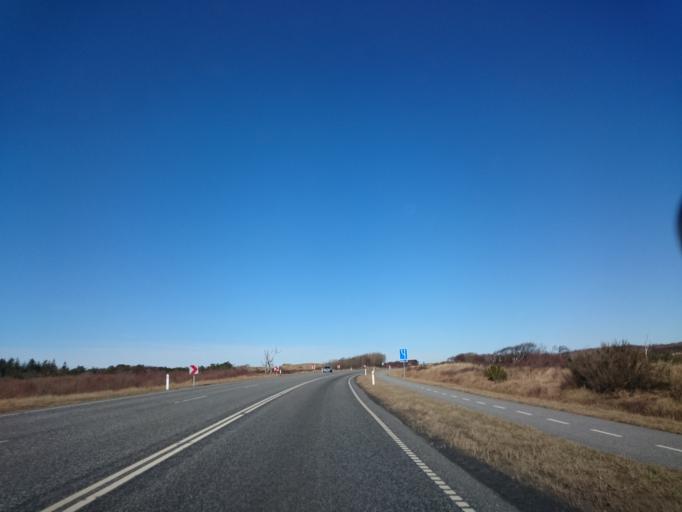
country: DK
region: North Denmark
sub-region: Frederikshavn Kommune
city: Skagen
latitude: 57.6711
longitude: 10.4546
